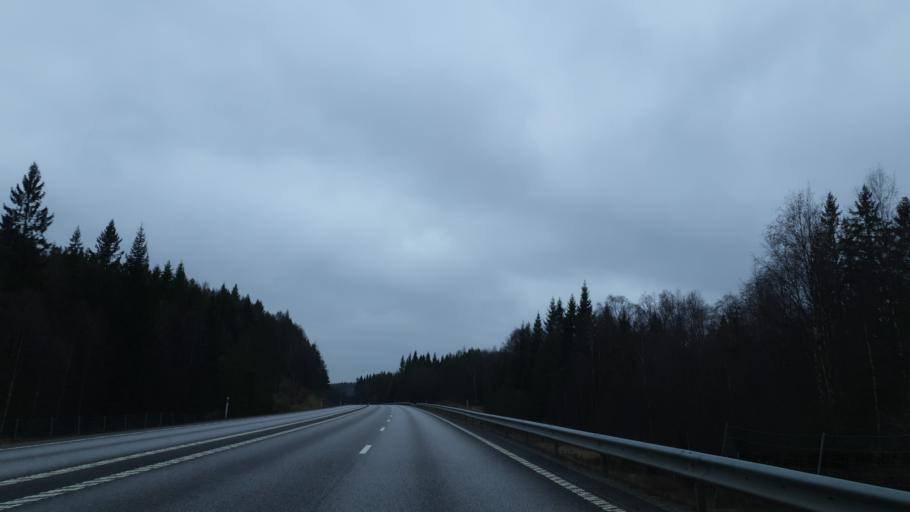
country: SE
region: Vaestra Goetaland
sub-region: Boras Kommun
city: Viskafors
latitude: 57.6229
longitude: 12.8857
